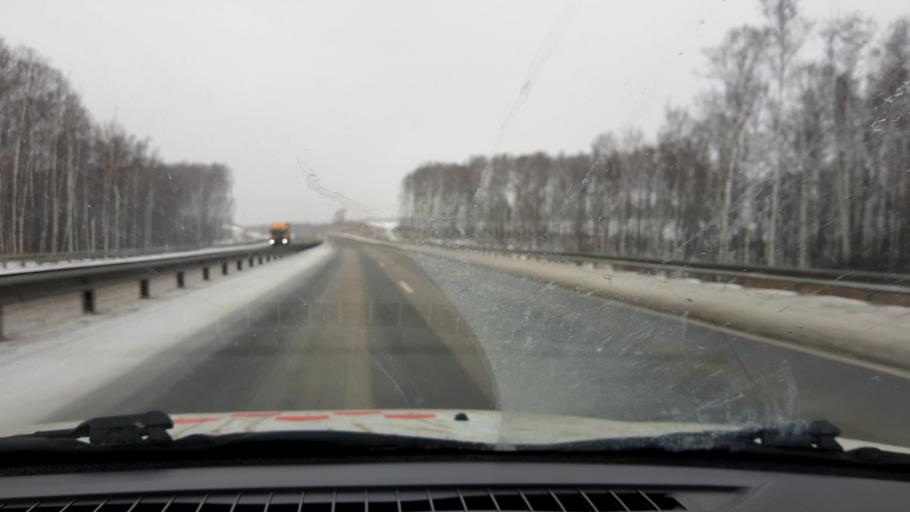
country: RU
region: Nizjnij Novgorod
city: Kstovo
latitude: 56.0990
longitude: 44.0600
